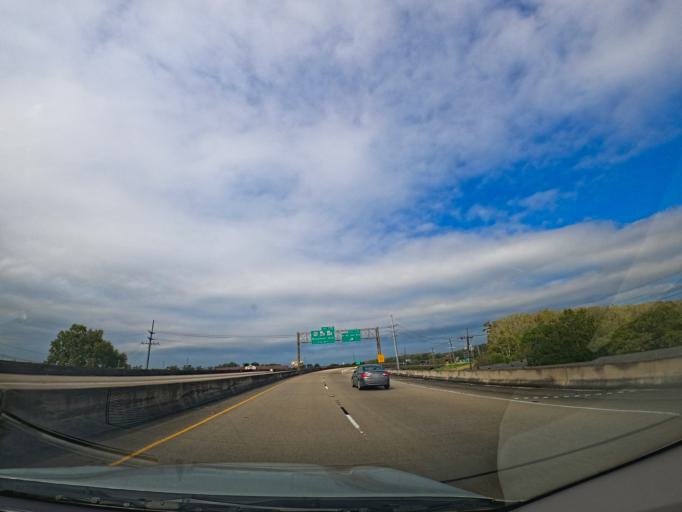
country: US
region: Louisiana
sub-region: Saint Mary Parish
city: Morgan City
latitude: 29.6966
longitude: -91.1786
